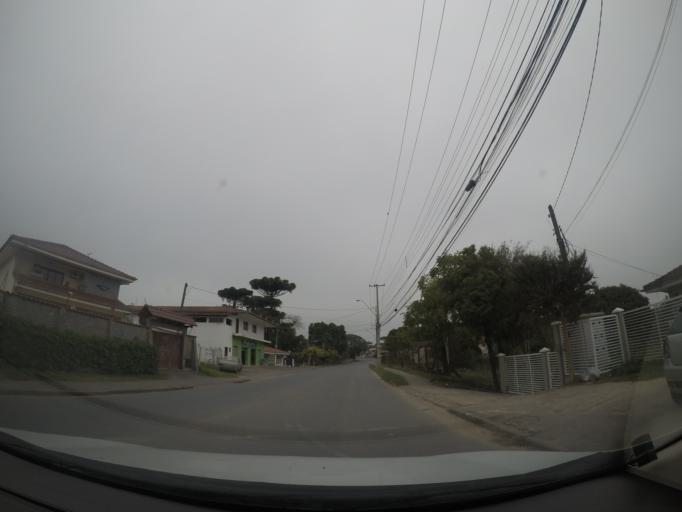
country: BR
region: Parana
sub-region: Almirante Tamandare
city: Almirante Tamandare
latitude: -25.3449
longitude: -49.2562
